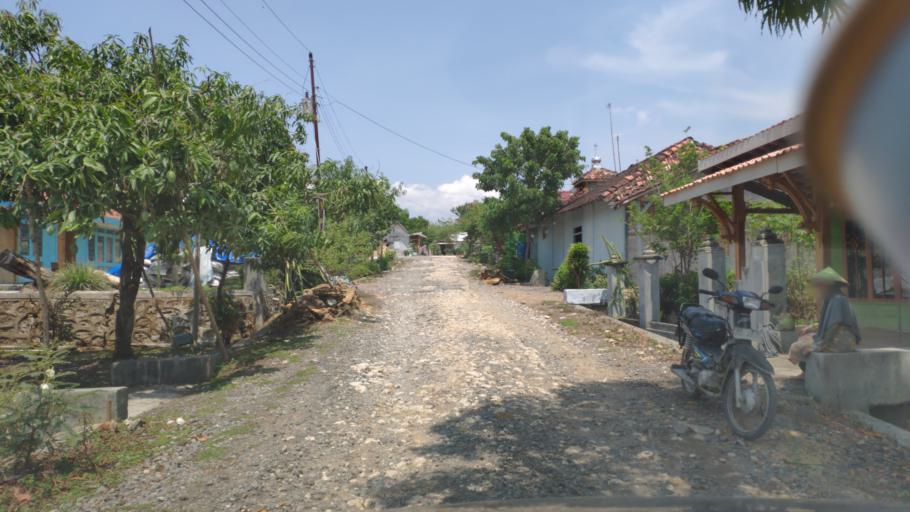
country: ID
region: Central Java
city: Balong Wetan
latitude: -7.0020
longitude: 111.2584
